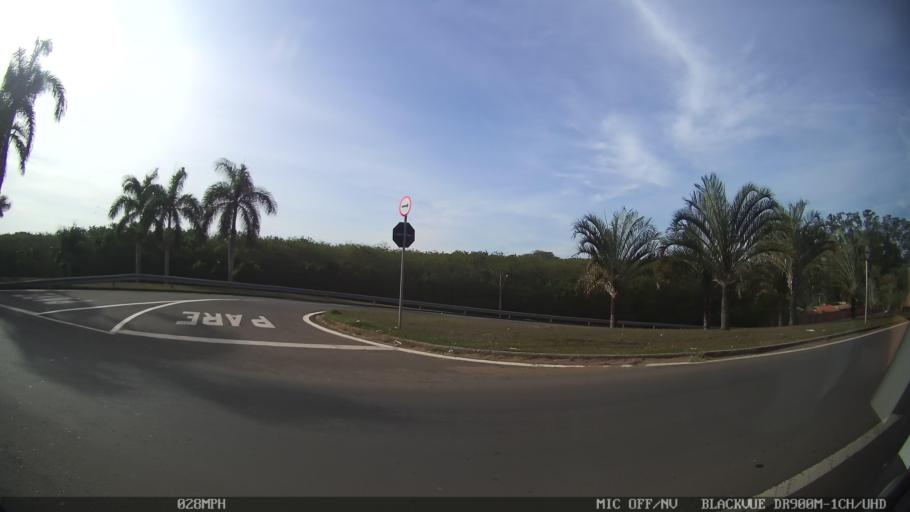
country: BR
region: Sao Paulo
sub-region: Piracicaba
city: Piracicaba
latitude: -22.7055
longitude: -47.6772
